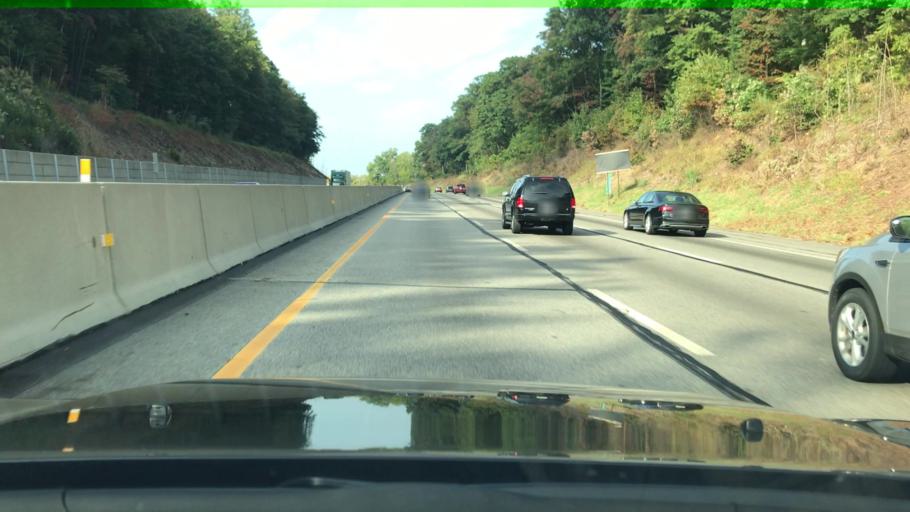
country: US
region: Pennsylvania
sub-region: Montgomery County
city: Plymouth Meeting
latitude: 40.1202
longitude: -75.2511
